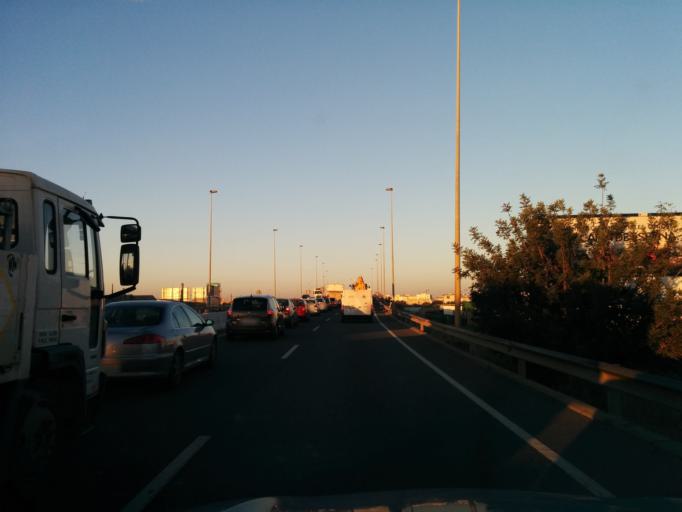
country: ES
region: Andalusia
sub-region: Provincia de Sevilla
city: Sevilla
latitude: 37.3687
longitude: -5.9380
